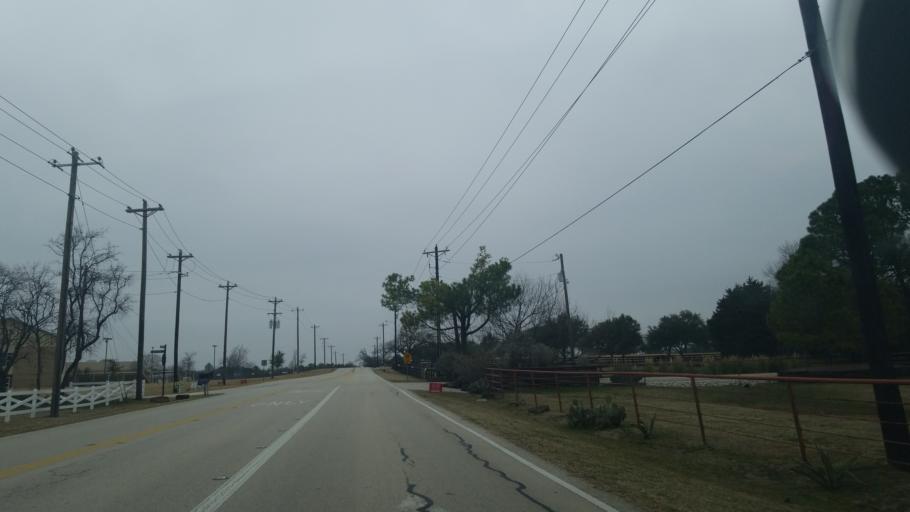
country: US
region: Texas
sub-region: Denton County
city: Copper Canyon
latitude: 33.1178
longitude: -97.1216
